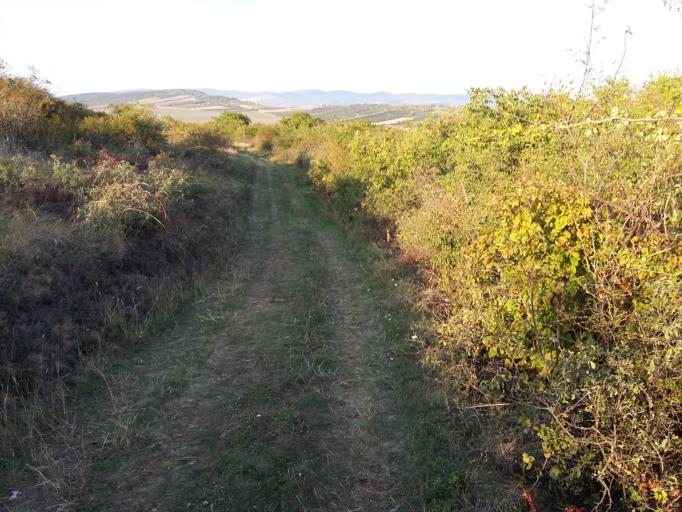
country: HU
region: Borsod-Abauj-Zemplen
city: Bekecs
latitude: 48.1565
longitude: 21.1720
